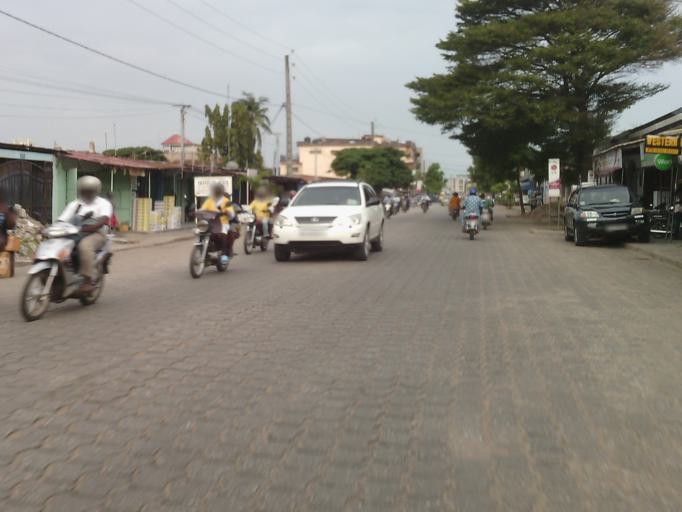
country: BJ
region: Littoral
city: Cotonou
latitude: 6.3876
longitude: 2.3803
